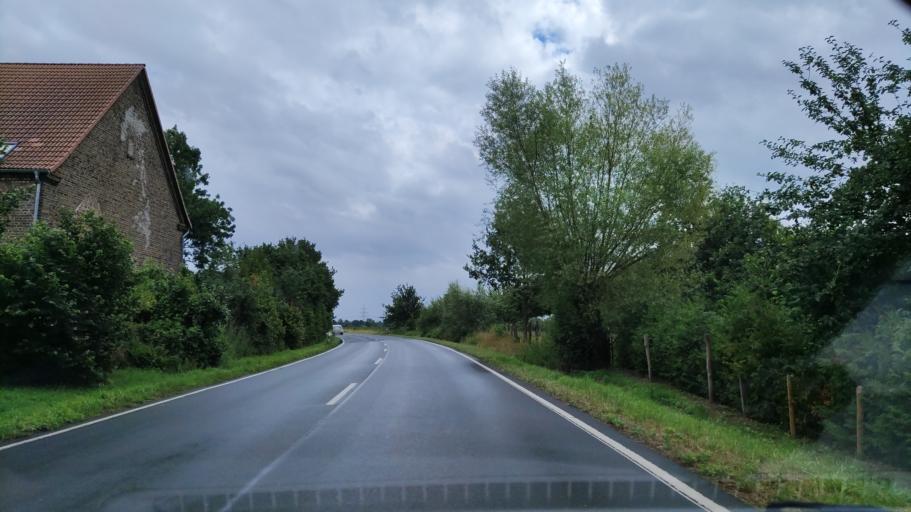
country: DE
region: North Rhine-Westphalia
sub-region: Regierungsbezirk Arnsberg
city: Welver
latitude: 51.6538
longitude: 7.9268
